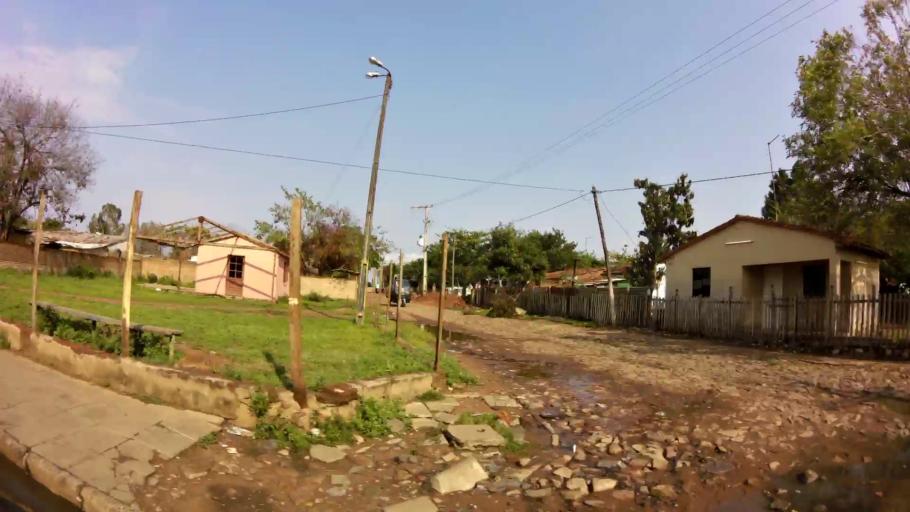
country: PY
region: Asuncion
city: Asuncion
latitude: -25.3065
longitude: -57.6673
